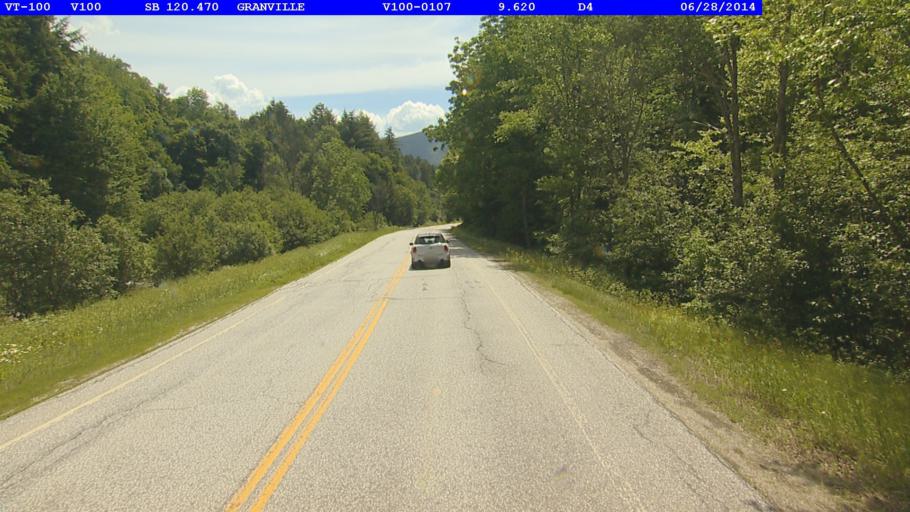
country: US
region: Vermont
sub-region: Washington County
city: Northfield
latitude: 44.0606
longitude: -72.8508
